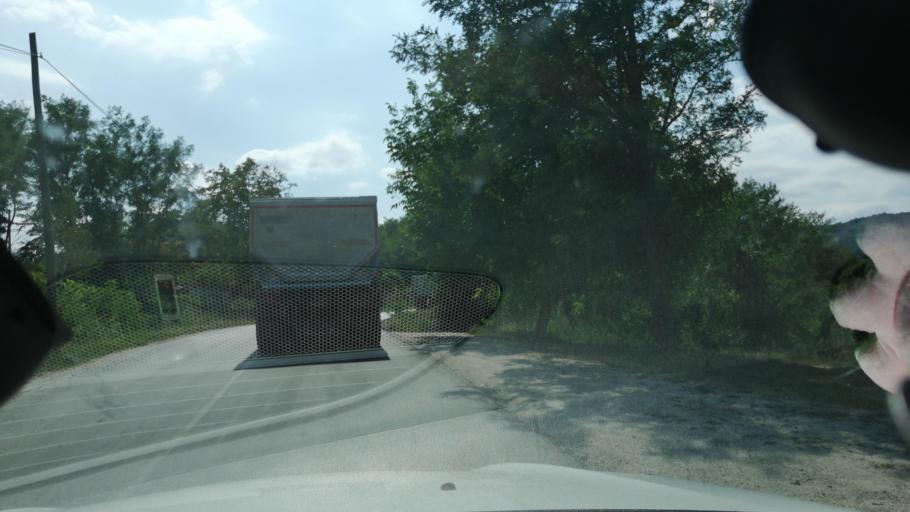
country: RS
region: Central Serbia
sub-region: Moravicki Okrug
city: Cacak
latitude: 43.8603
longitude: 20.3119
